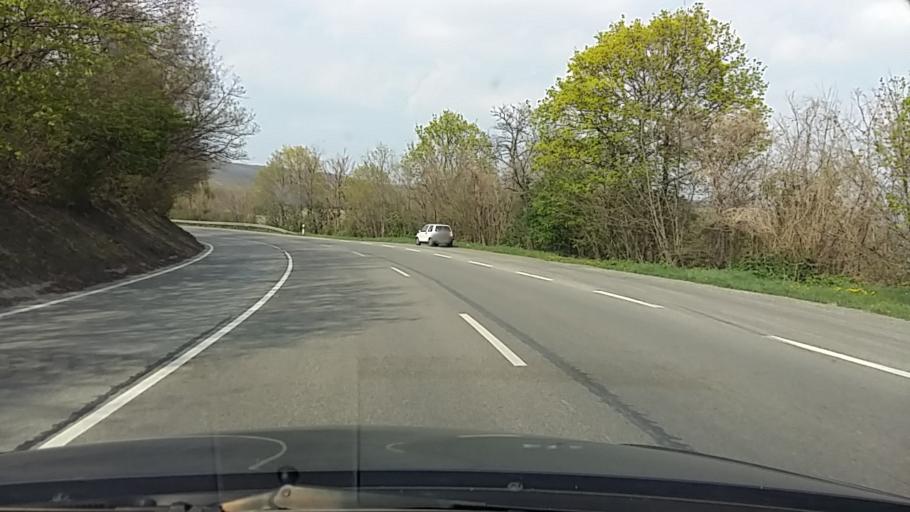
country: HU
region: Baranya
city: Pecs
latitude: 46.1215
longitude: 18.2615
